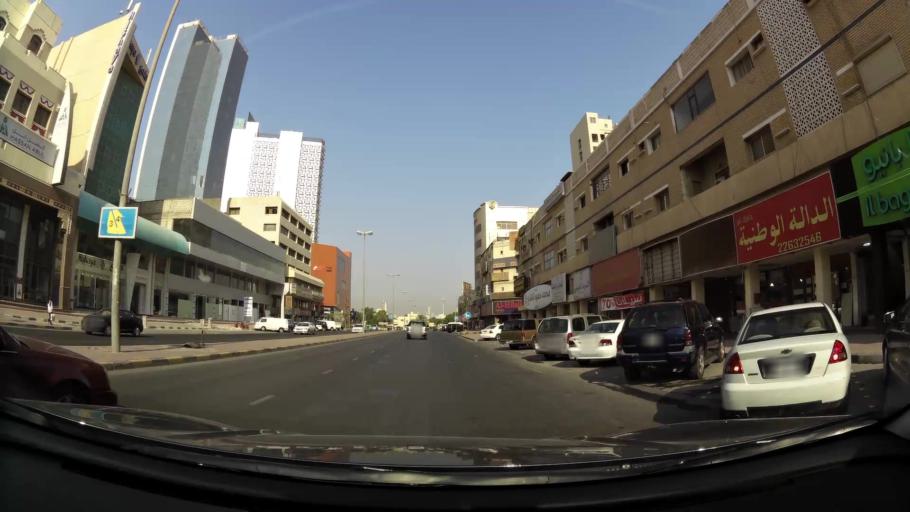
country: KW
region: Muhafazat Hawalli
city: Hawalli
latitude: 29.3462
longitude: 48.0140
